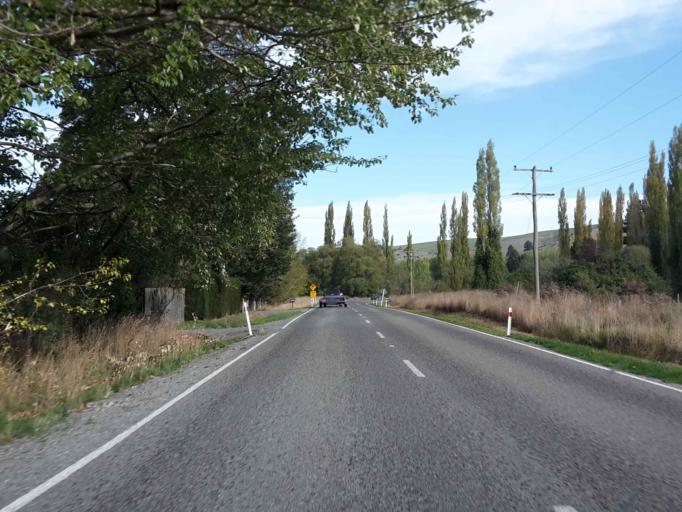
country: NZ
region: Canterbury
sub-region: Timaru District
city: Pleasant Point
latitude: -44.0715
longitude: 170.9479
